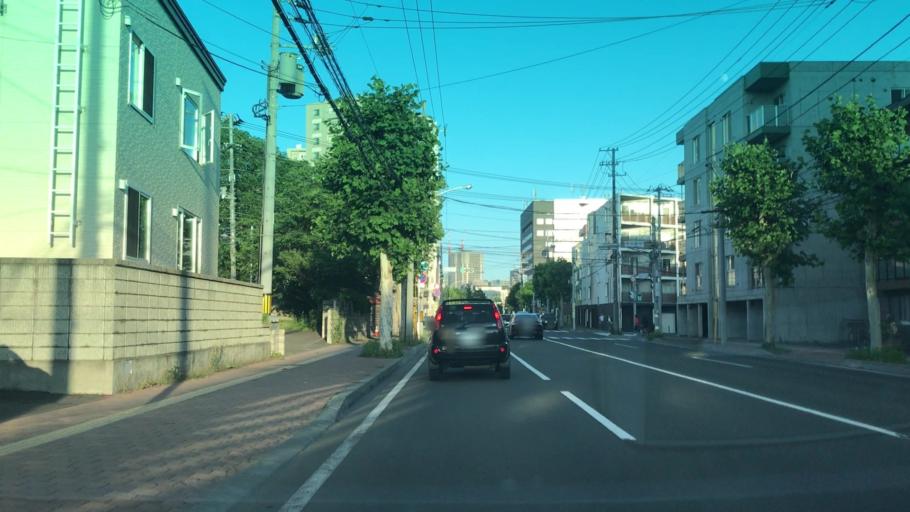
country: JP
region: Hokkaido
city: Sapporo
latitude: 43.0729
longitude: 141.3289
